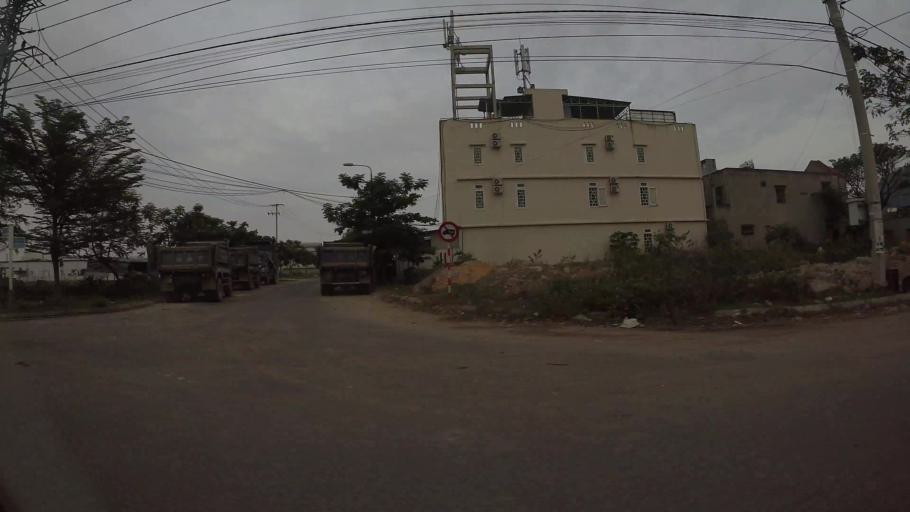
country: VN
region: Da Nang
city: Lien Chieu
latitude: 16.0786
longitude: 108.1212
